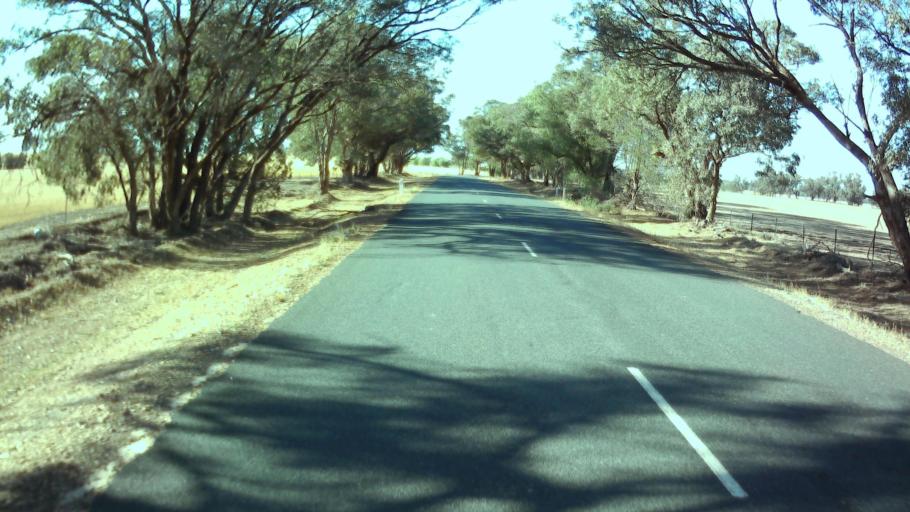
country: AU
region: New South Wales
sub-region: Weddin
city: Grenfell
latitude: -33.9746
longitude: 148.1410
